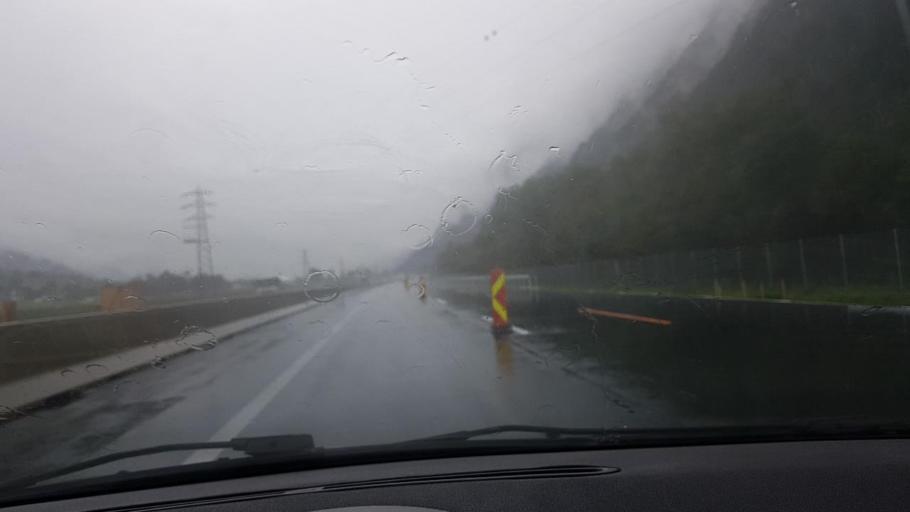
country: AT
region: Tyrol
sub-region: Politischer Bezirk Imst
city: Rietz
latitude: 47.2959
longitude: 11.0366
